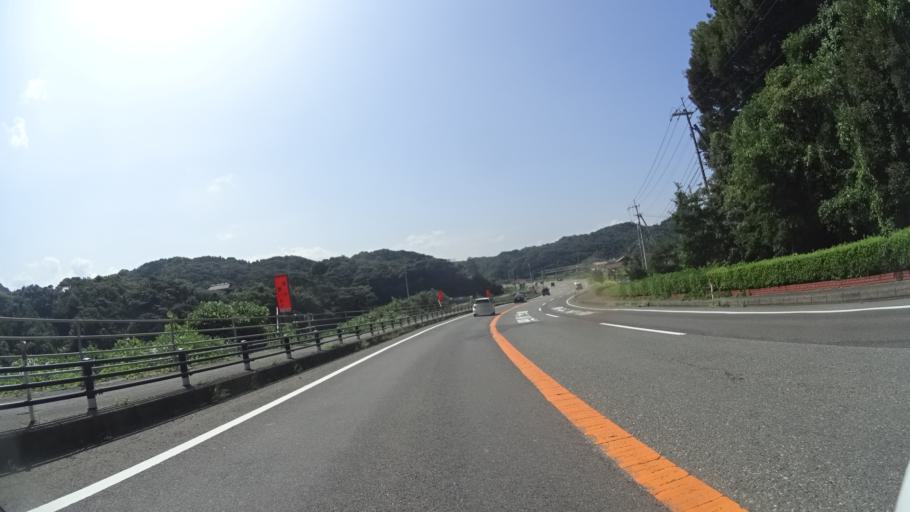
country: JP
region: Shimane
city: Masuda
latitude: 34.7343
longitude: 131.8741
